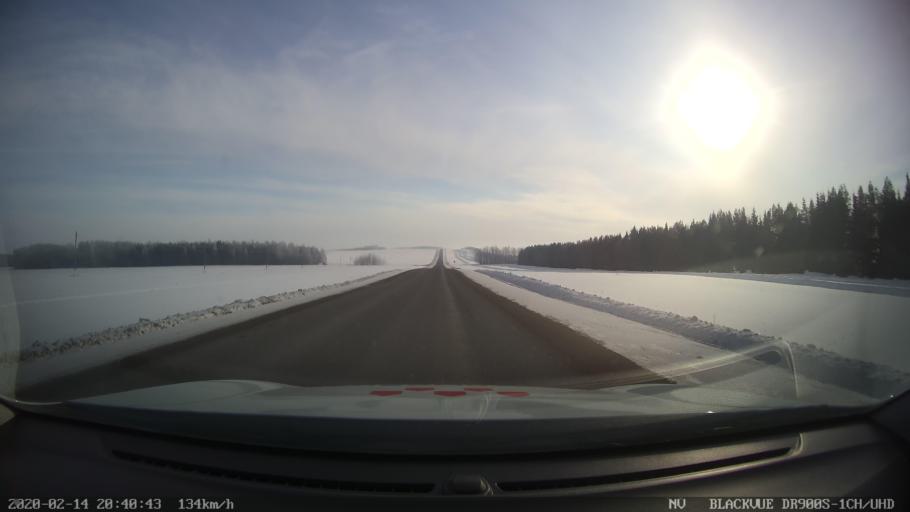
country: RU
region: Tatarstan
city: Kuybyshevskiy Zaton
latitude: 55.3374
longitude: 49.0985
